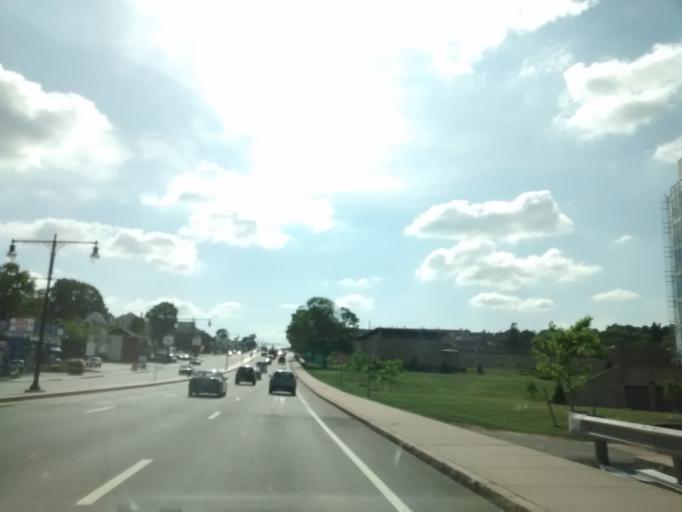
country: US
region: Massachusetts
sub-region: Worcester County
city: Hamilton
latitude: 42.2740
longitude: -71.7616
